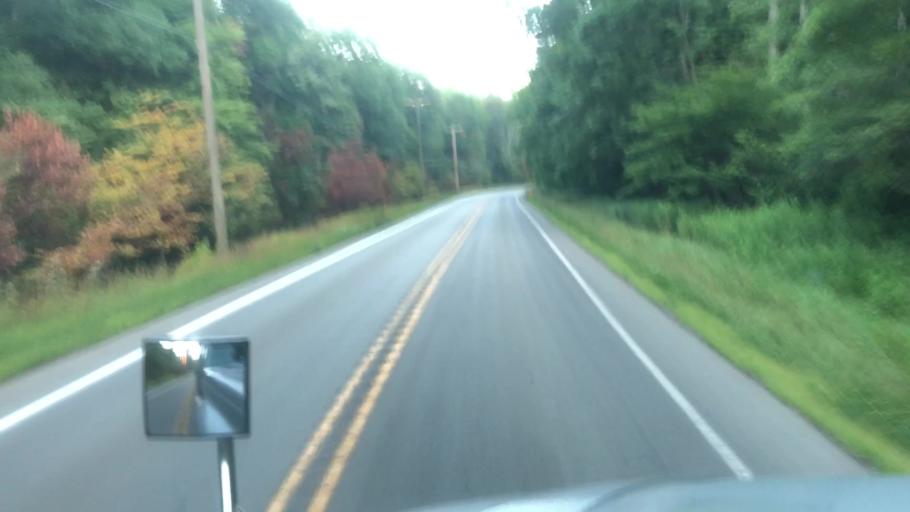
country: US
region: Pennsylvania
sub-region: Venango County
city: Hasson Heights
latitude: 41.4808
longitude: -79.6641
